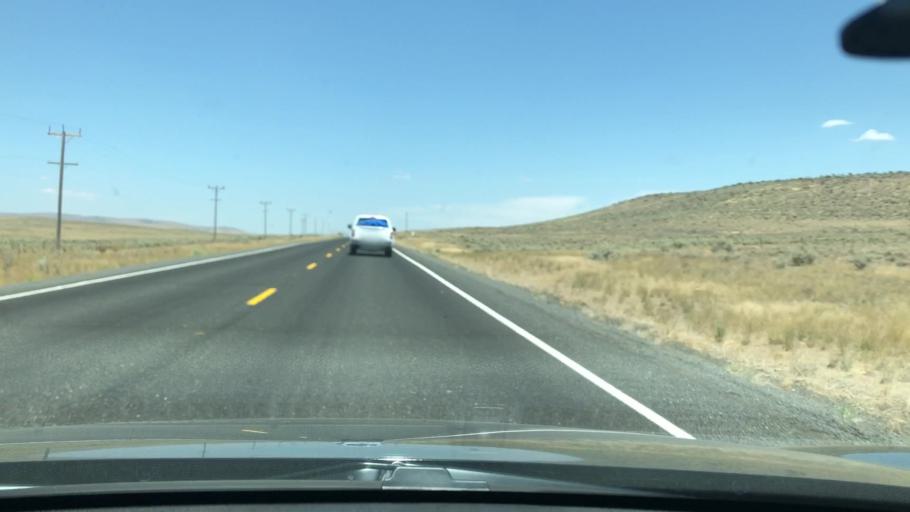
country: US
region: Idaho
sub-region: Owyhee County
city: Murphy
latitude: 43.0564
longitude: -117.0699
